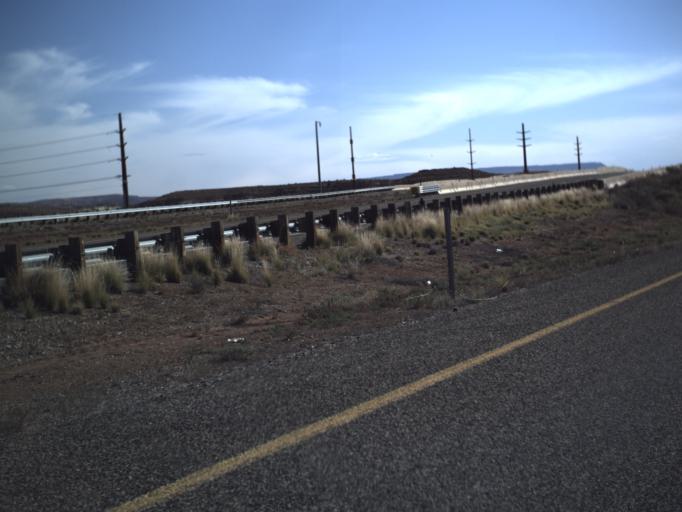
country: US
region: Utah
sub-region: Washington County
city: Saint George
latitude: 37.0004
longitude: -113.5630
